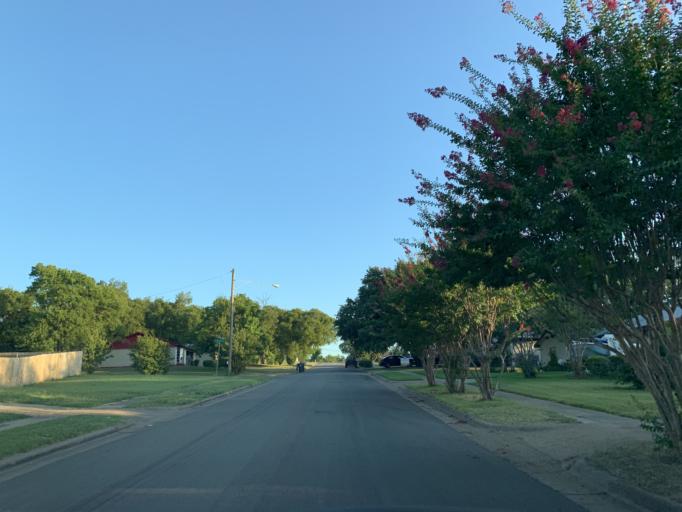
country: US
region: Texas
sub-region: Dallas County
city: Lancaster
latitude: 32.6643
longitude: -96.8041
